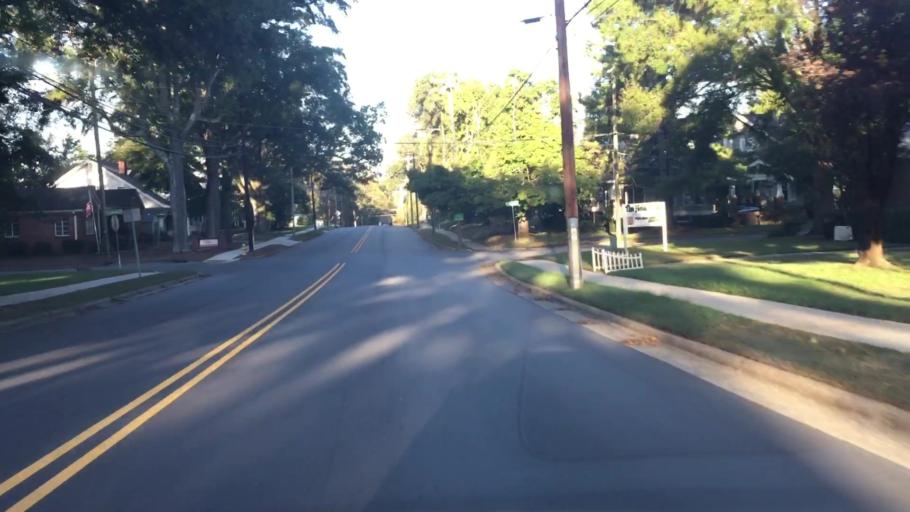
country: US
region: North Carolina
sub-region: Iredell County
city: Mooresville
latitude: 35.5794
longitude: -80.8055
